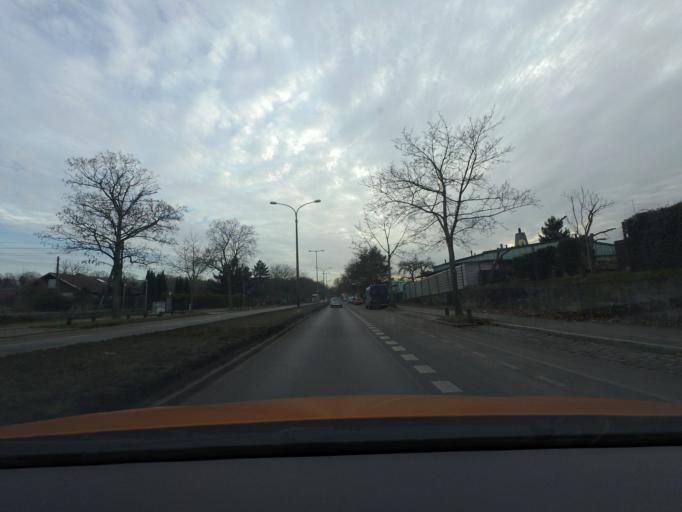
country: DE
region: Berlin
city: Niederschonhausen
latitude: 52.5985
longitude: 13.4028
